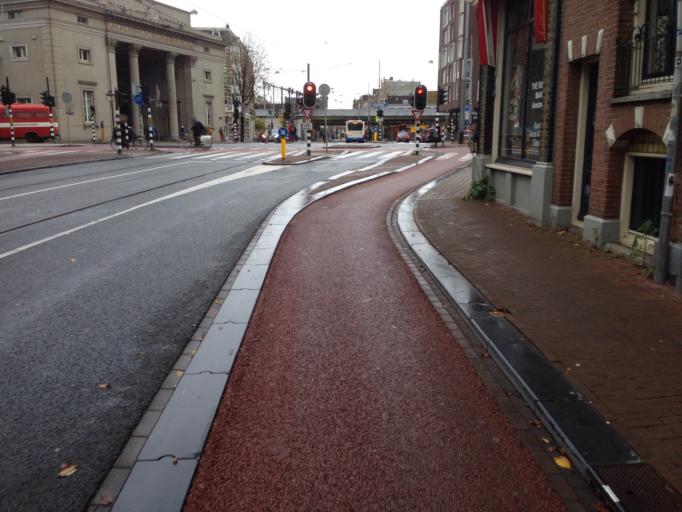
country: NL
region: North Holland
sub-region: Gemeente Amsterdam
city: Amsterdam
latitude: 52.3843
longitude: 4.8829
